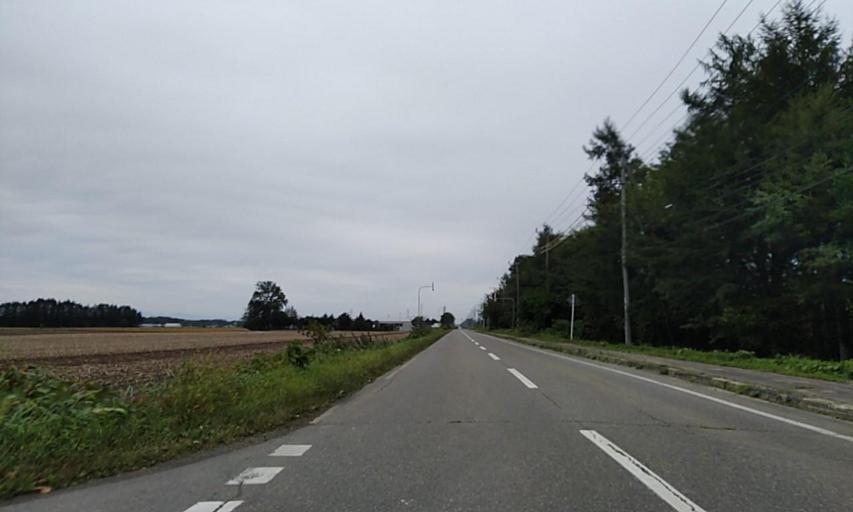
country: JP
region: Hokkaido
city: Obihiro
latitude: 42.6758
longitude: 143.1175
